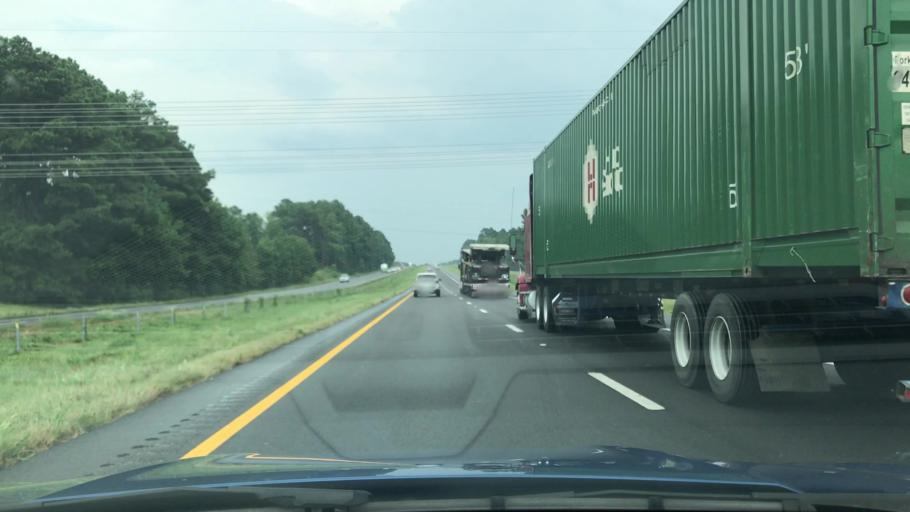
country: US
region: Texas
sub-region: Harrison County
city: Hallsville
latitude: 32.4855
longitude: -94.4915
